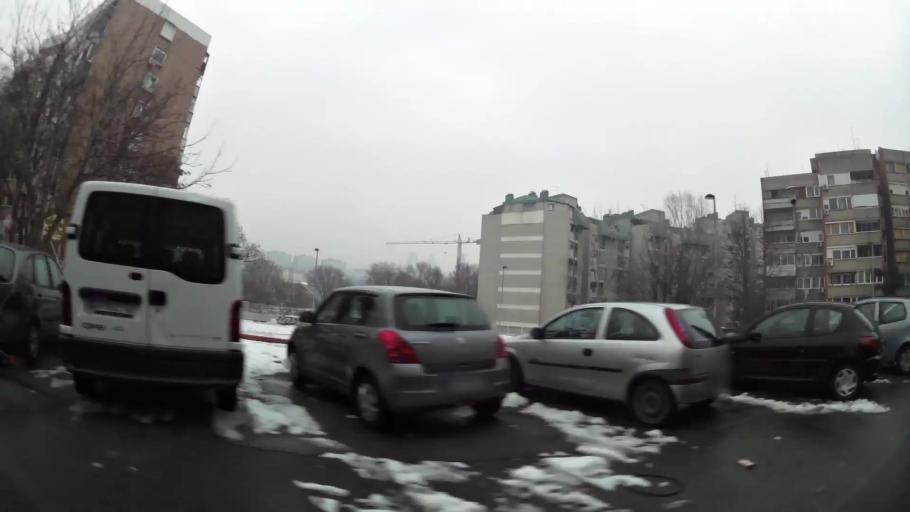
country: RS
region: Central Serbia
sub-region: Belgrade
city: Vozdovac
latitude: 44.7765
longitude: 20.4979
